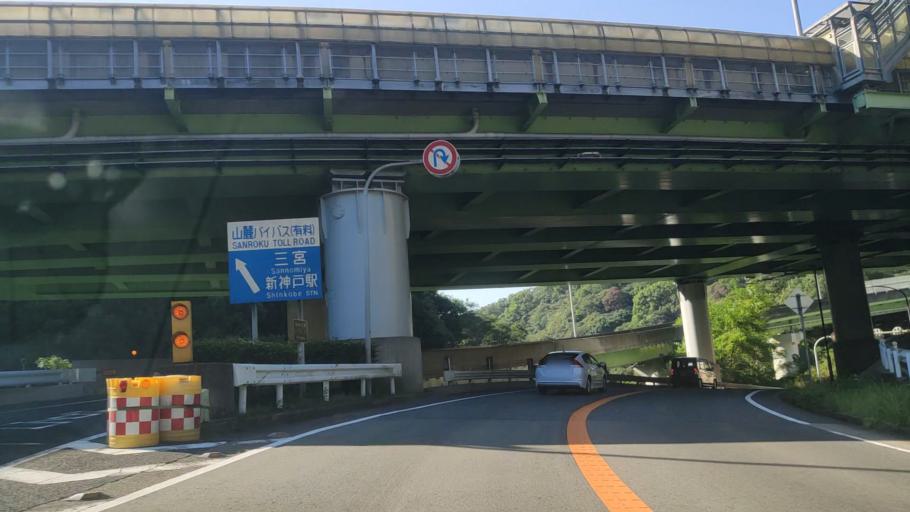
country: JP
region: Hyogo
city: Kobe
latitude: 34.6996
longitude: 135.1652
